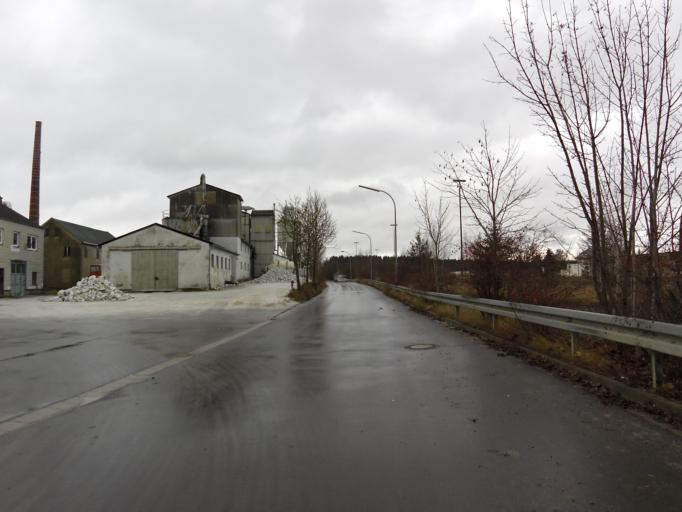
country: DE
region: Bavaria
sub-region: Upper Franconia
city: Wunsiedel
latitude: 50.0504
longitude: 12.0352
